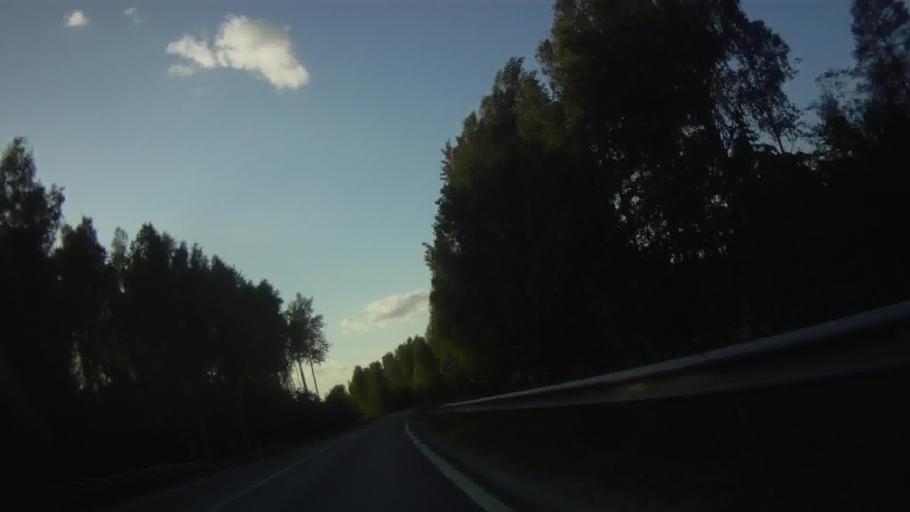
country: LV
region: Livani
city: Livani
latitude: 56.5321
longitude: 26.1406
